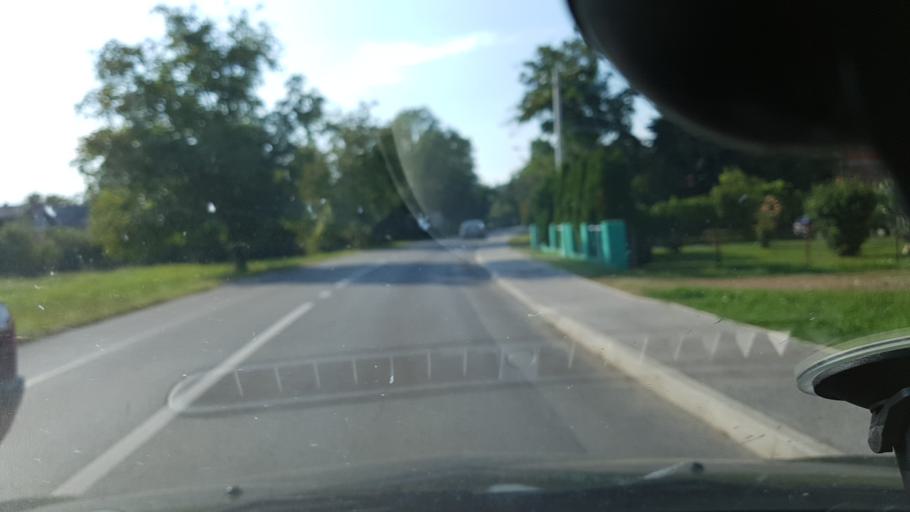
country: HR
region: Zagrebacka
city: Bregana
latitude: 45.8799
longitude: 15.7261
